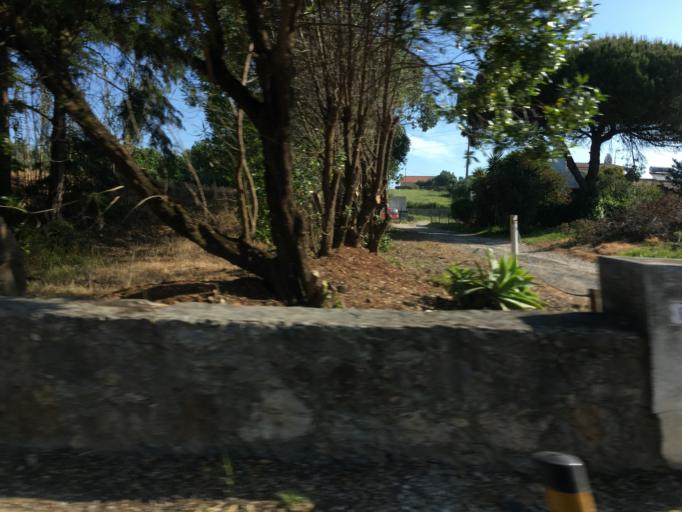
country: PT
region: Lisbon
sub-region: Cascais
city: Parede
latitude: 38.7371
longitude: -9.3582
